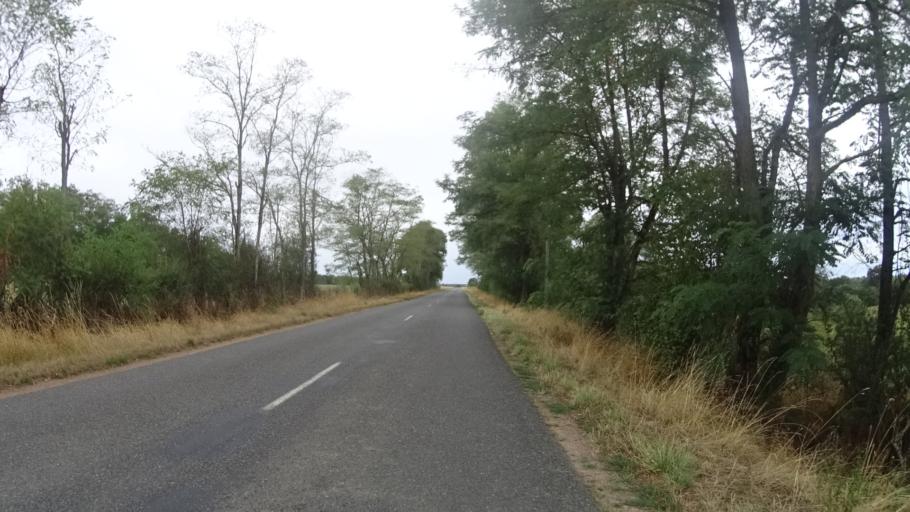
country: FR
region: Bourgogne
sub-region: Departement de la Nievre
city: Decize
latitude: 46.7818
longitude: 3.5354
